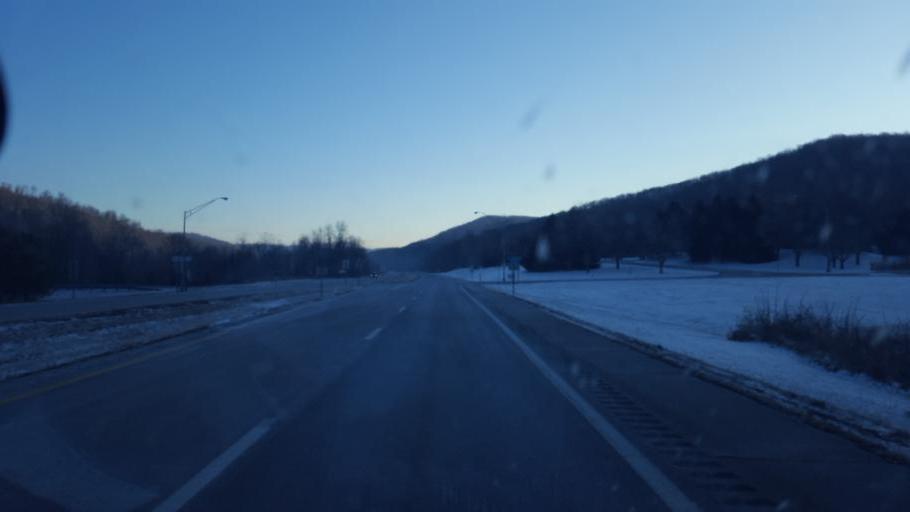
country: US
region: Ohio
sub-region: Adams County
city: Peebles
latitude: 39.0417
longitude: -83.2329
